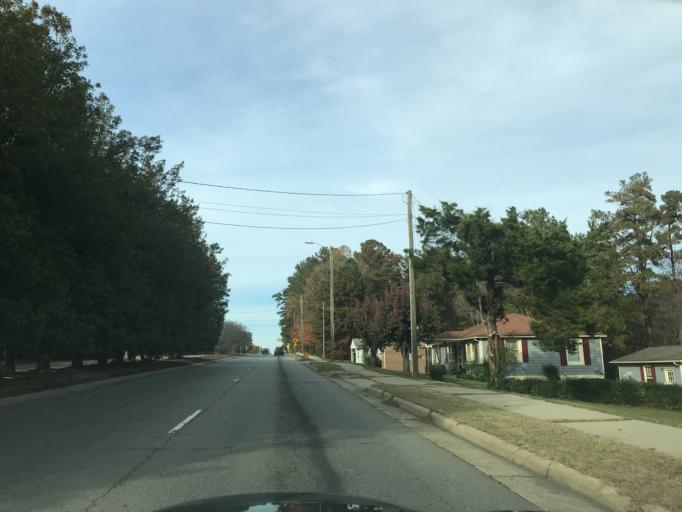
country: US
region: North Carolina
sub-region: Wake County
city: West Raleigh
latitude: 35.8522
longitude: -78.6803
